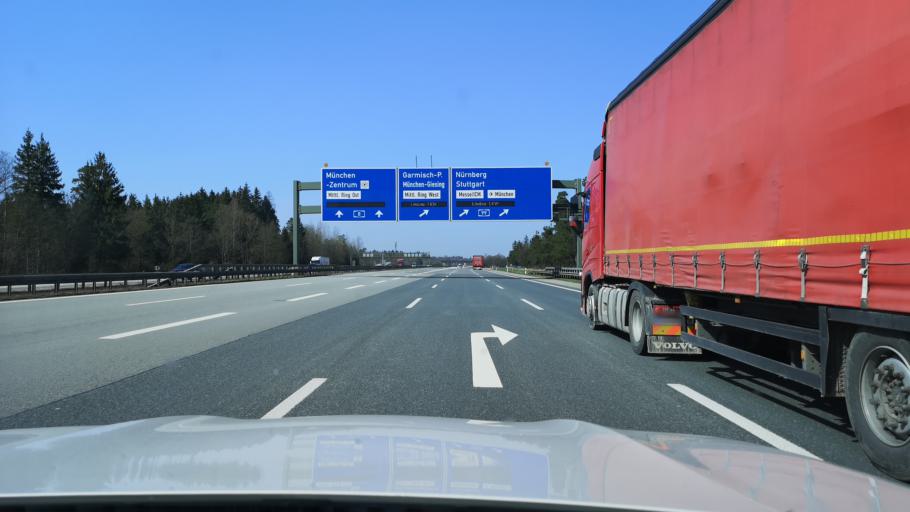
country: DE
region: Bavaria
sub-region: Upper Bavaria
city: Brunnthal
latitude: 48.0123
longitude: 11.6667
